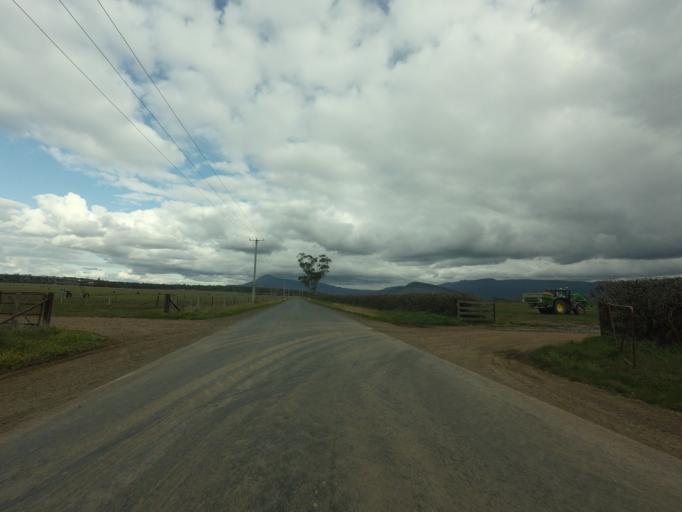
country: AU
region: Tasmania
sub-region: Northern Midlands
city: Longford
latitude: -41.7907
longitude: 147.1129
